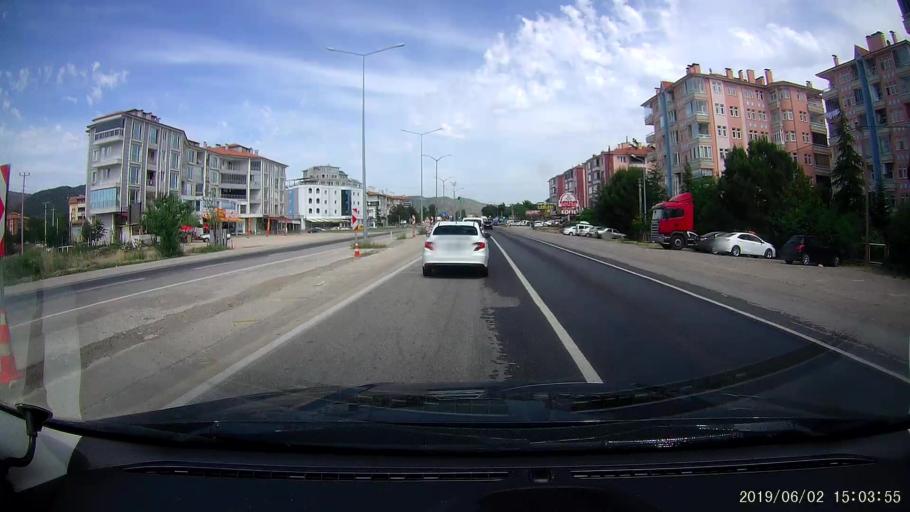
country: TR
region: Corum
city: Osmancik
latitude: 40.9788
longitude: 34.7886
